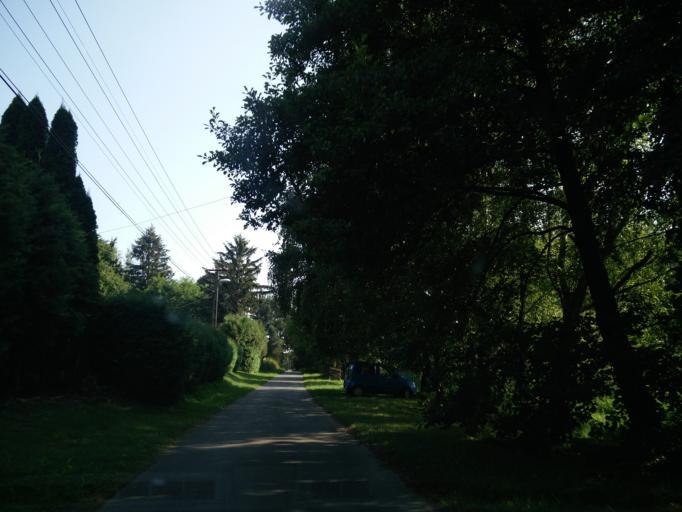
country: HU
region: Zala
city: Zalaegerszeg
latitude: 46.8737
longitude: 16.8489
